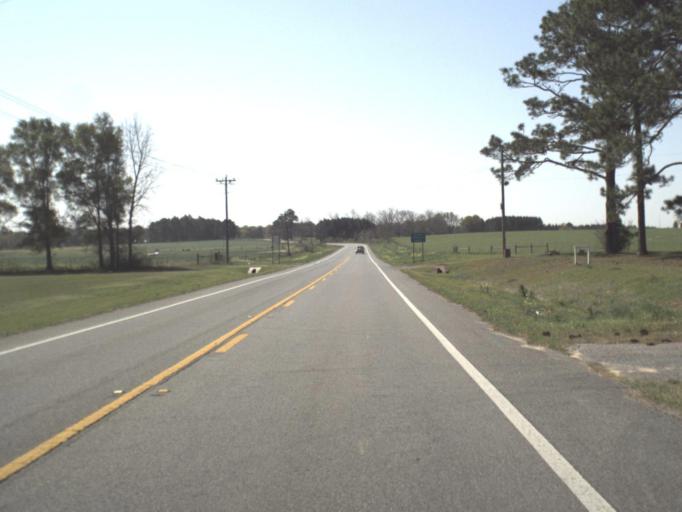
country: US
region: Florida
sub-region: Washington County
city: Chipley
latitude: 30.8307
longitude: -85.5037
